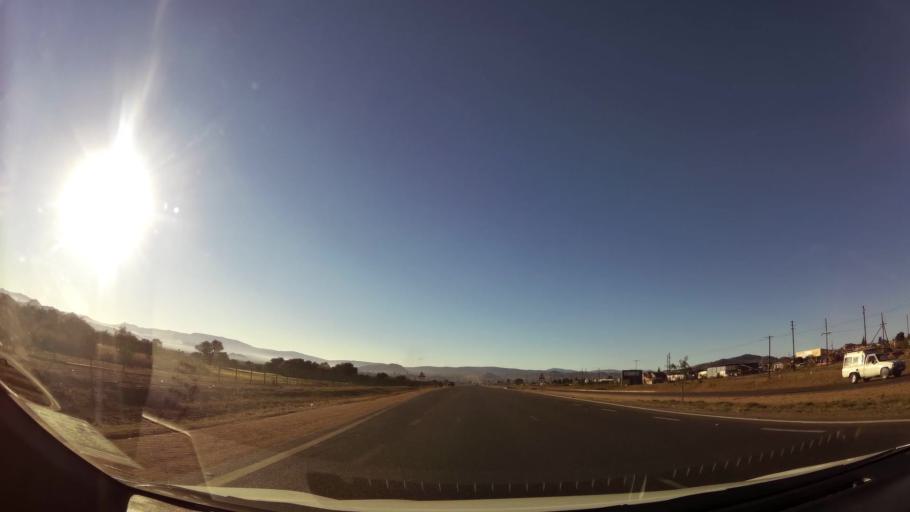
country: ZA
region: Limpopo
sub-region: Capricorn District Municipality
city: Mankoeng
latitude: -23.8997
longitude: 29.7386
